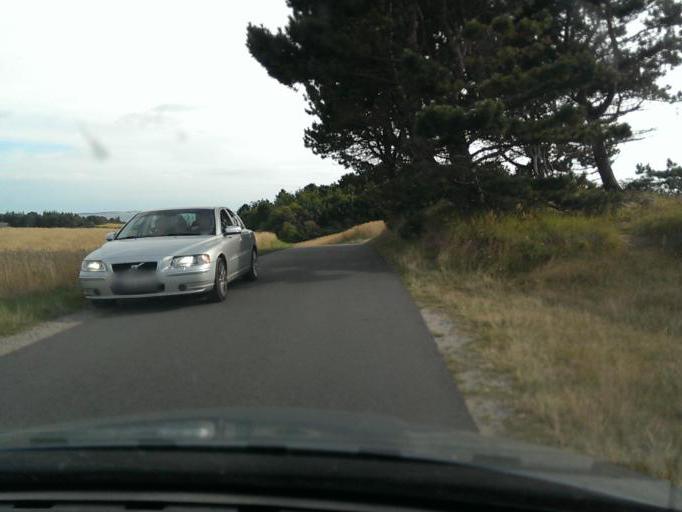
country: DK
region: Central Jutland
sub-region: Syddjurs Kommune
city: Ronde
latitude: 56.1107
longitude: 10.5056
